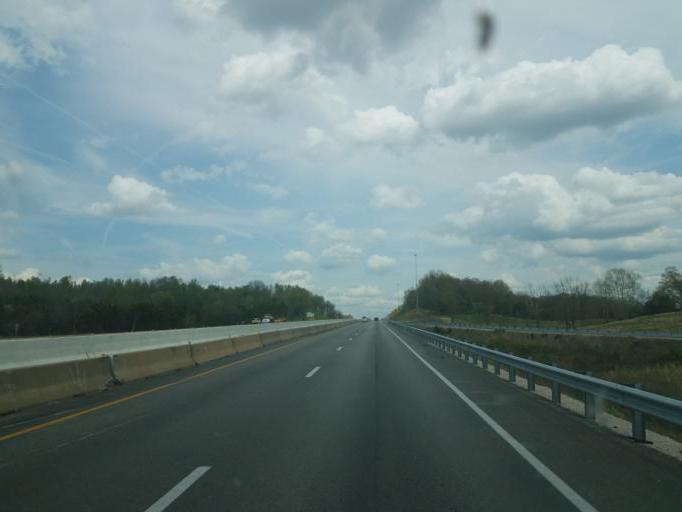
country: US
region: Kentucky
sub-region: Hart County
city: Munfordville
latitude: 37.3814
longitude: -85.8876
